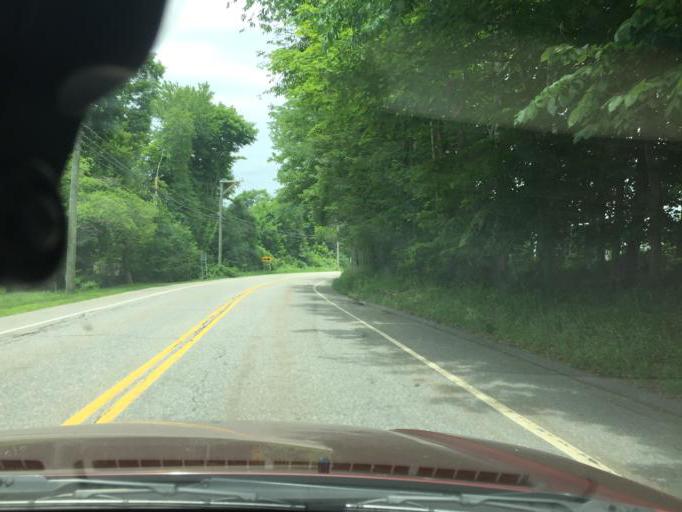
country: US
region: Connecticut
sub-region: Litchfield County
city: Litchfield
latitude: 41.7155
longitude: -73.2359
